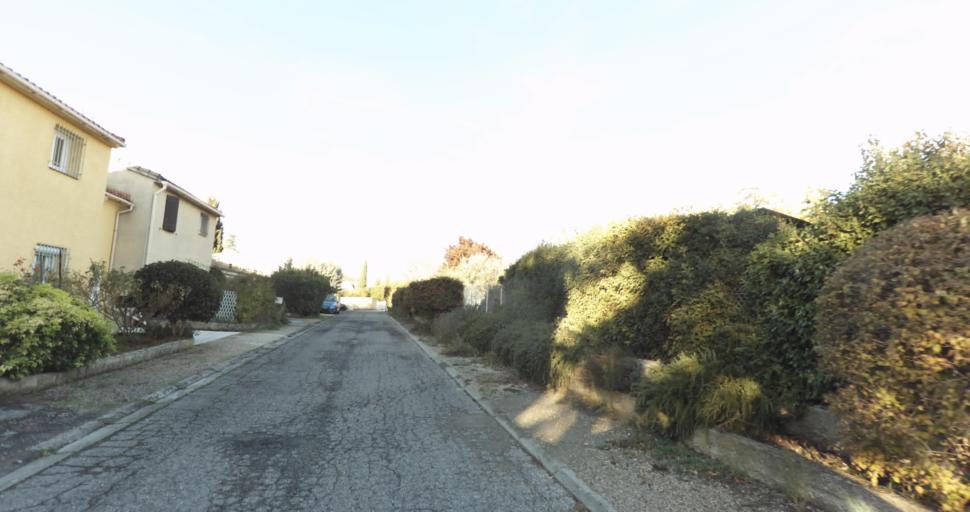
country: FR
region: Provence-Alpes-Cote d'Azur
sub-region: Departement des Bouches-du-Rhone
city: Venelles
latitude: 43.5961
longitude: 5.4831
